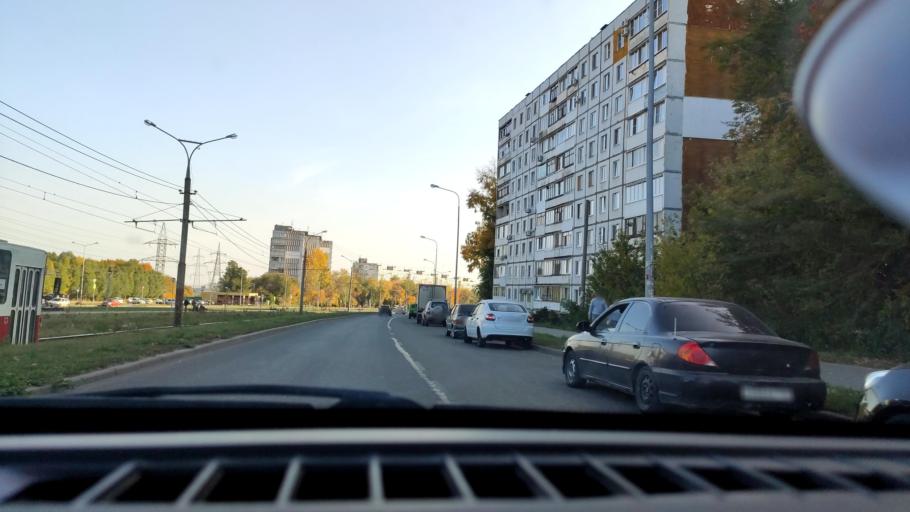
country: RU
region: Samara
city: Samara
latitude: 53.2575
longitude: 50.2441
